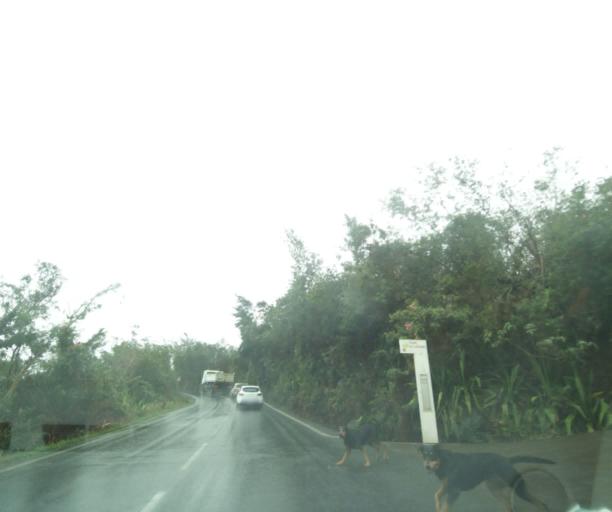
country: RE
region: Reunion
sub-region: Reunion
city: Saint-Paul
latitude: -21.0341
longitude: 55.2817
